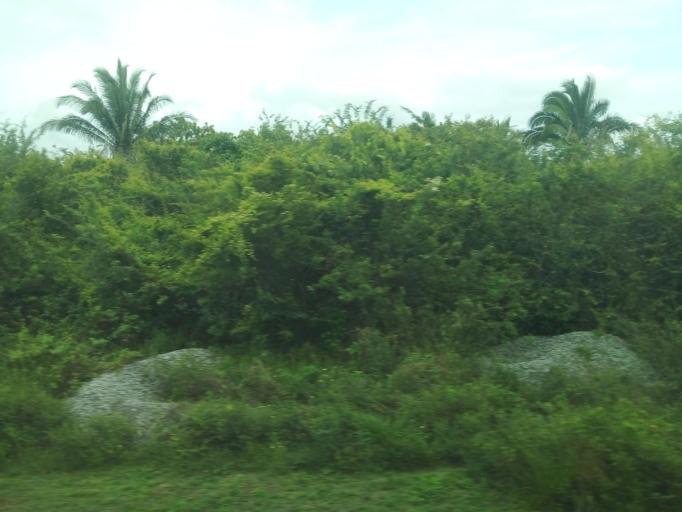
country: BR
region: Maranhao
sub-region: Itapecuru Mirim
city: Itapecuru Mirim
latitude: -3.2916
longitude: -44.4598
